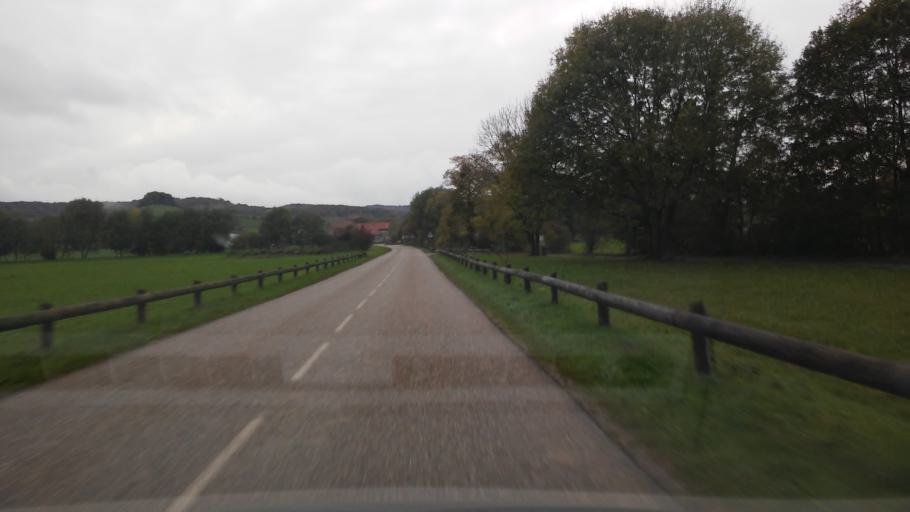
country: FR
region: Lorraine
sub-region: Departement de la Moselle
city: Boulay-Moselle
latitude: 49.1879
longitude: 6.4559
